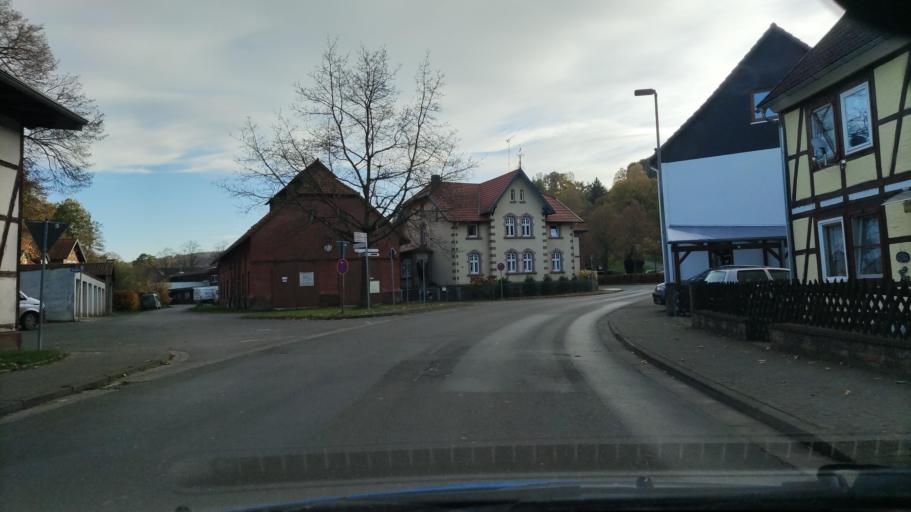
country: DE
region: Lower Saxony
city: Dassel
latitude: 51.7627
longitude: 9.7581
